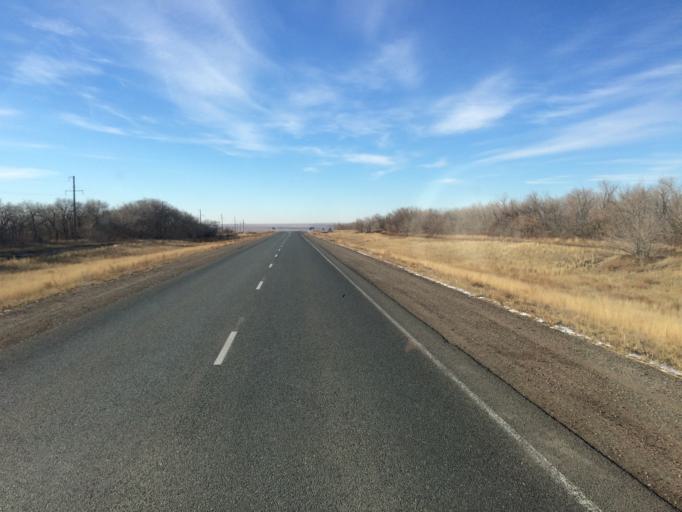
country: KZ
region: Aqtoebe
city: Aqtobe
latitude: 50.2475
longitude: 56.7940
